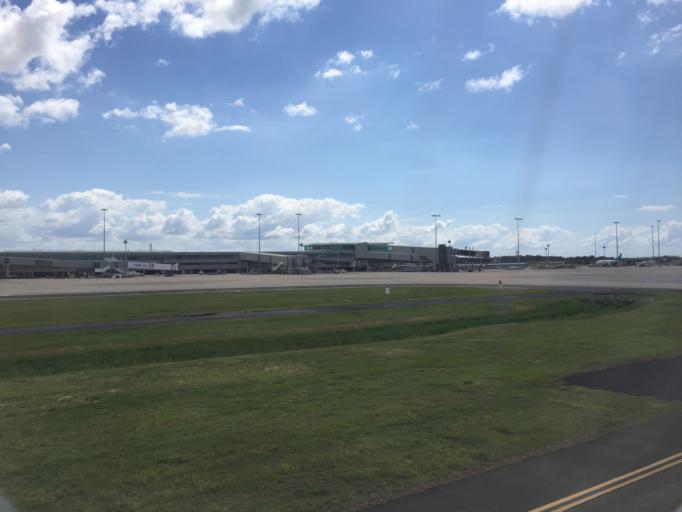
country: AU
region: Queensland
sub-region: Brisbane
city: Wynnum
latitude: -27.4035
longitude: 153.1142
